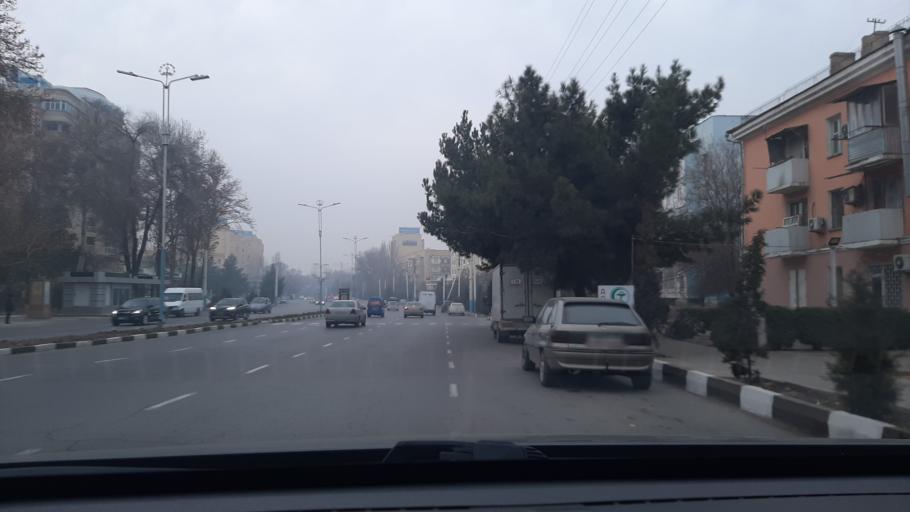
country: TJ
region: Viloyati Sughd
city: Khujand
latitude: 40.2658
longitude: 69.6540
